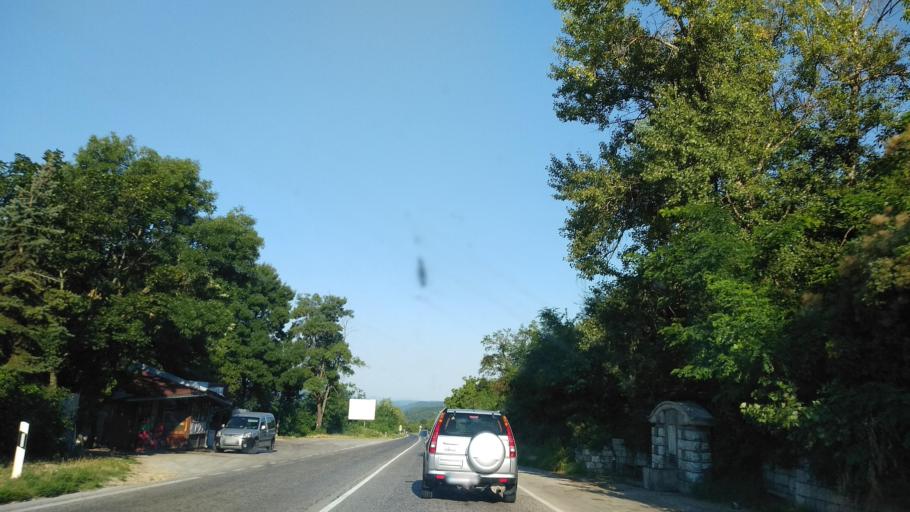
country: BG
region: Lovech
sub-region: Obshtina Lovech
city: Lovech
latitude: 43.0480
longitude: 24.7776
